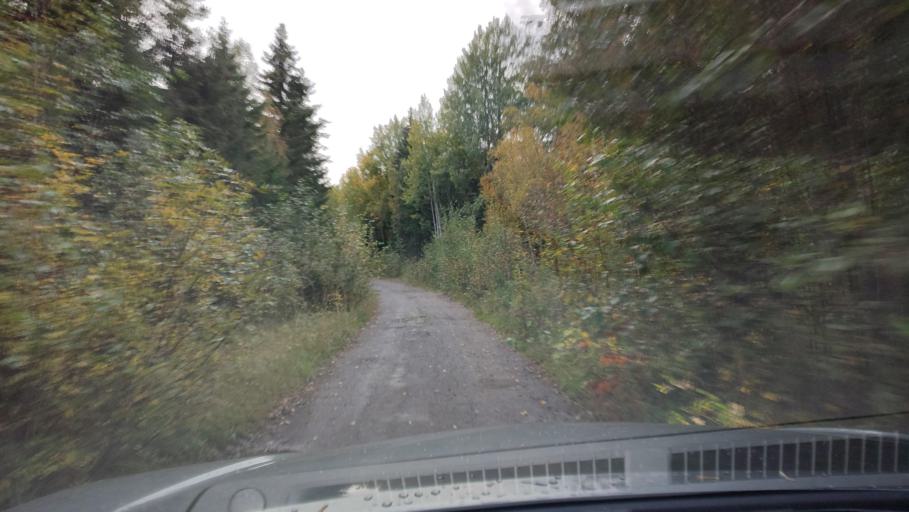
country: FI
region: Ostrobothnia
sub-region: Sydosterbotten
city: Kristinestad
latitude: 62.2723
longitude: 21.4453
